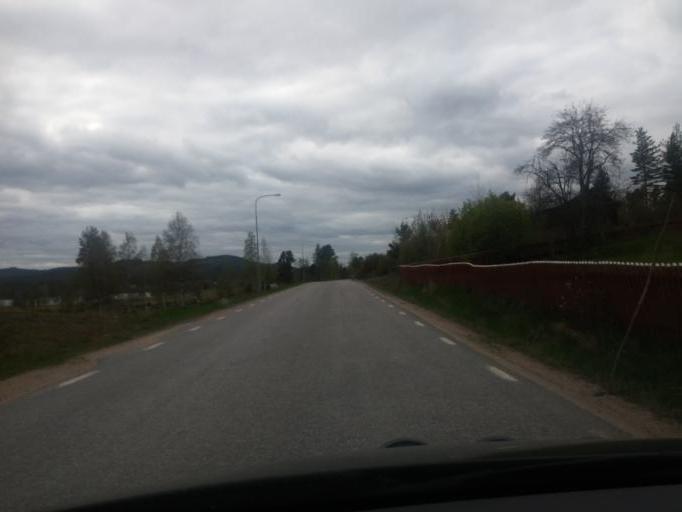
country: SE
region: Gaevleborg
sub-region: Ljusdals Kommun
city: Ljusdal
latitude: 61.8567
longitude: 16.0337
